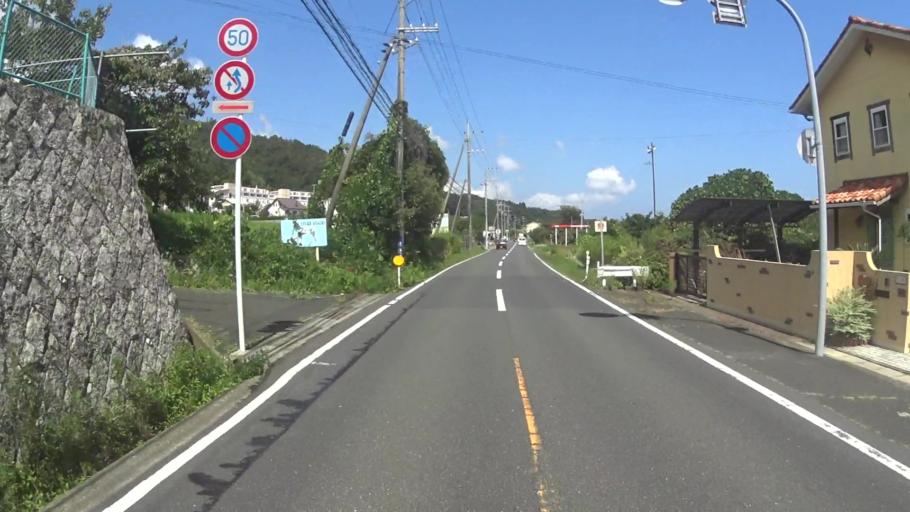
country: JP
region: Kyoto
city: Miyazu
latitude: 35.5891
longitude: 135.2073
